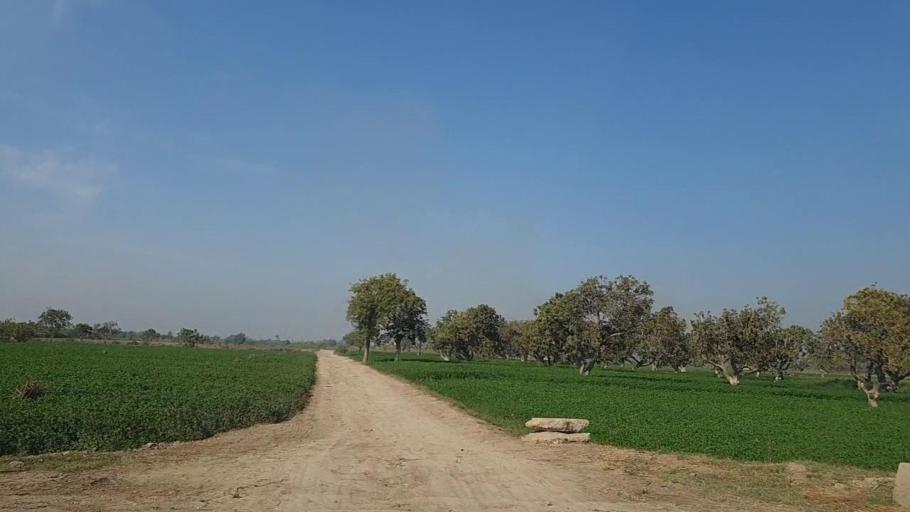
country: PK
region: Sindh
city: Mirpur Khas
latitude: 25.4999
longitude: 68.9922
